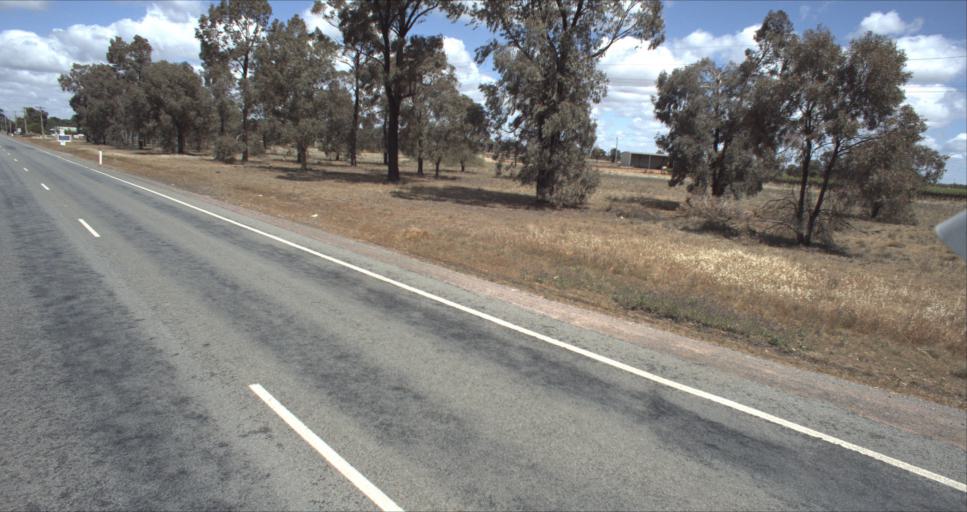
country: AU
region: New South Wales
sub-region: Murrumbidgee Shire
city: Darlington Point
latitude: -34.5081
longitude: 146.1868
